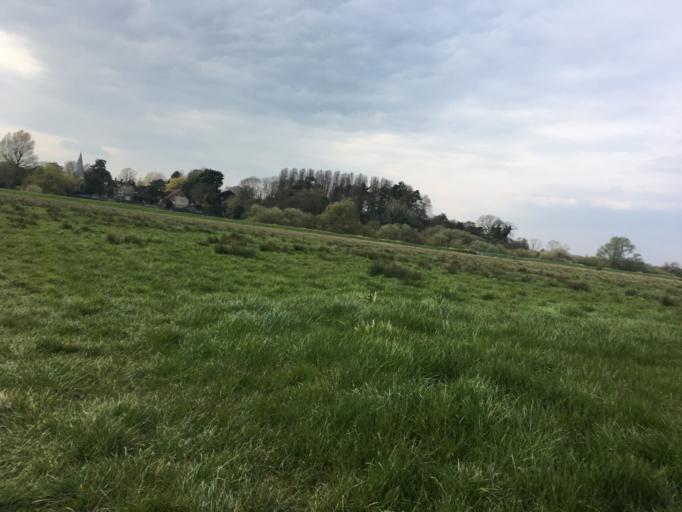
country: GB
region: England
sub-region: West Sussex
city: Arundel
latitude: 50.9073
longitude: -0.5507
